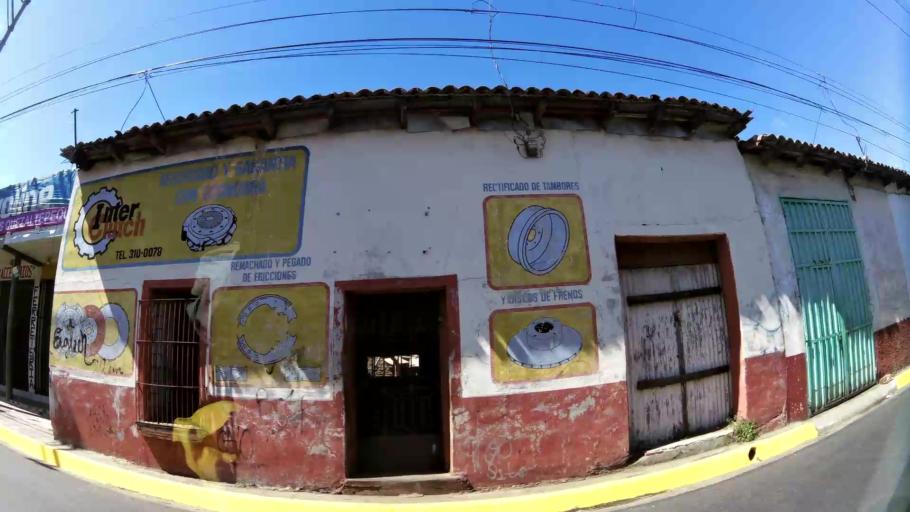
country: SV
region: La Libertad
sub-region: Distrito de Quezaltepeque
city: Quezaltepeque
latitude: 13.8330
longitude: -89.2750
